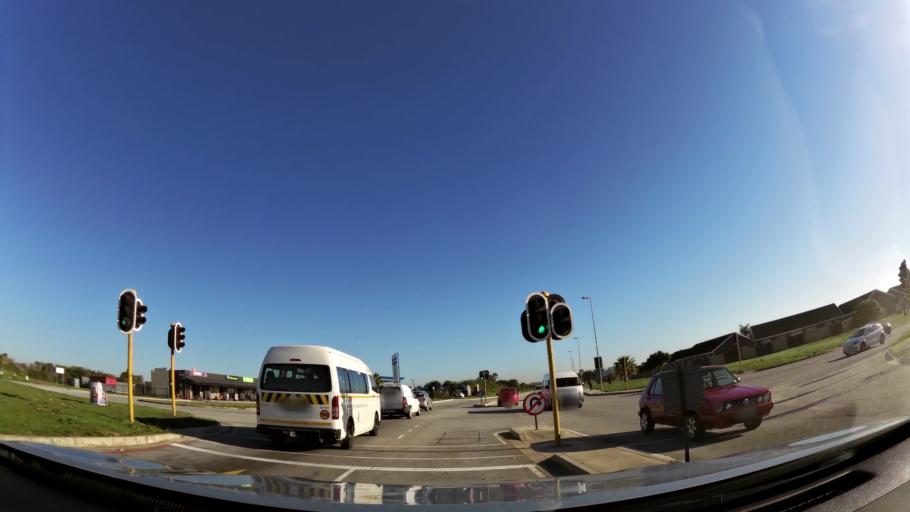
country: ZA
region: Eastern Cape
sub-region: Nelson Mandela Bay Metropolitan Municipality
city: Port Elizabeth
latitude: -33.9917
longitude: 25.6483
